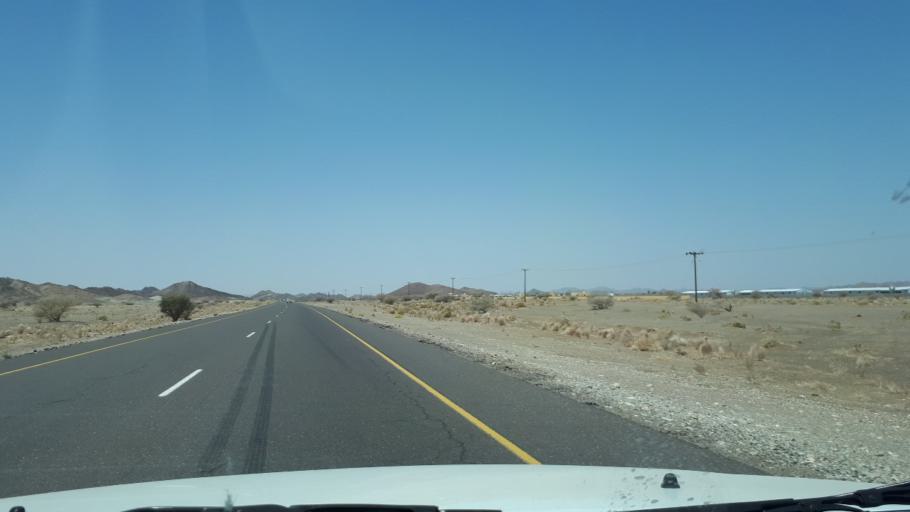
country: OM
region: Ash Sharqiyah
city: Ibra'
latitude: 22.6401
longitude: 58.4845
